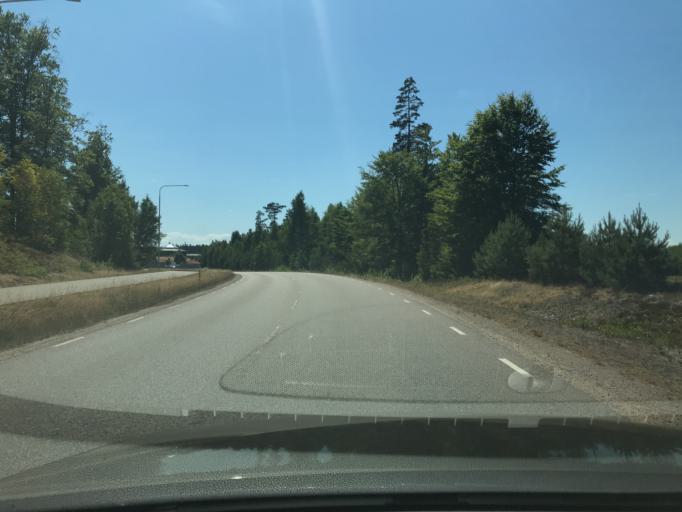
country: SE
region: Kronoberg
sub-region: Vaxjo Kommun
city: Vaexjoe
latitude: 56.9116
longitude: 14.8432
